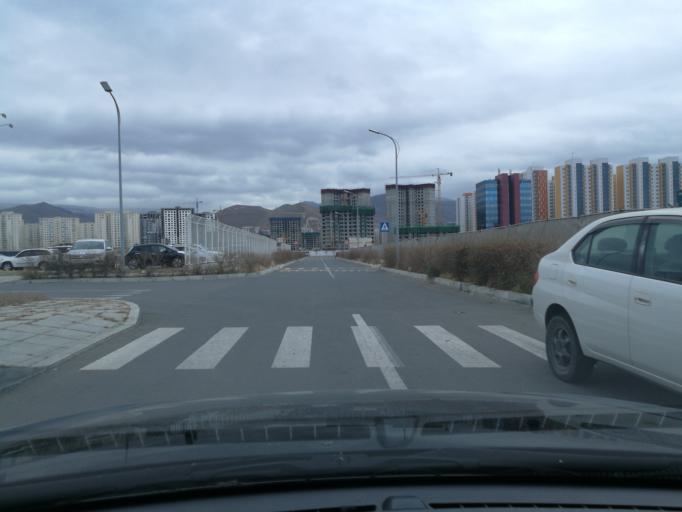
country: MN
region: Ulaanbaatar
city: Ulaanbaatar
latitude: 47.9011
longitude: 106.9254
